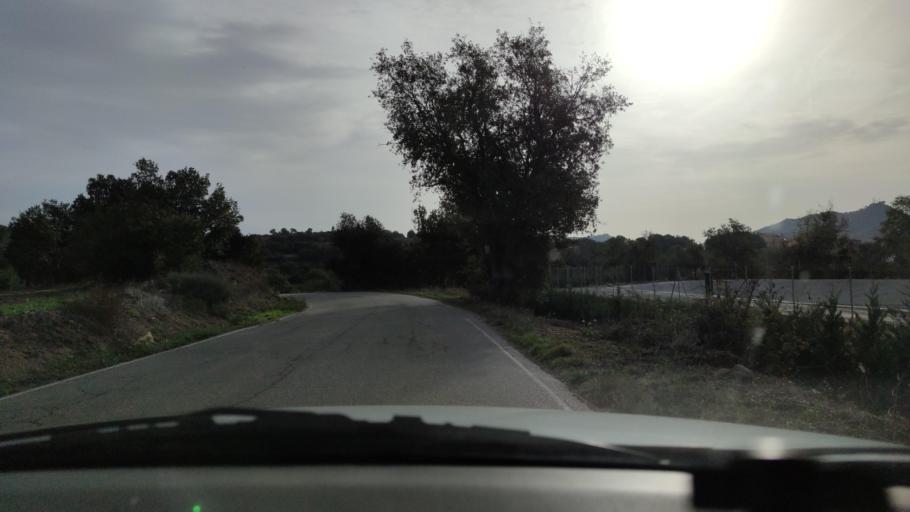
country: ES
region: Catalonia
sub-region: Provincia de Lleida
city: Artesa de Segre
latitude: 41.9074
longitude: 1.0389
